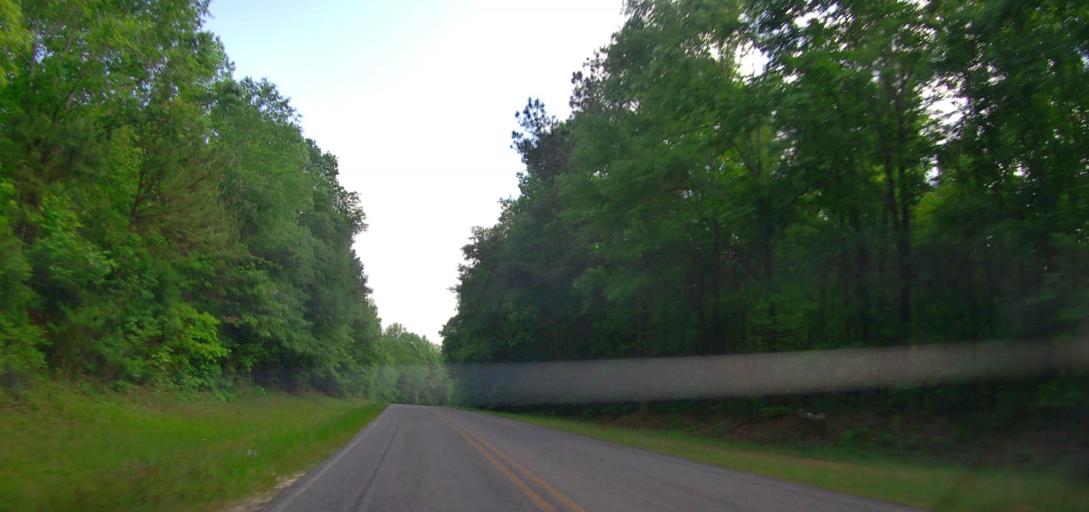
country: US
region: Georgia
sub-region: Laurens County
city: East Dublin
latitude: 32.6692
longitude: -82.8951
